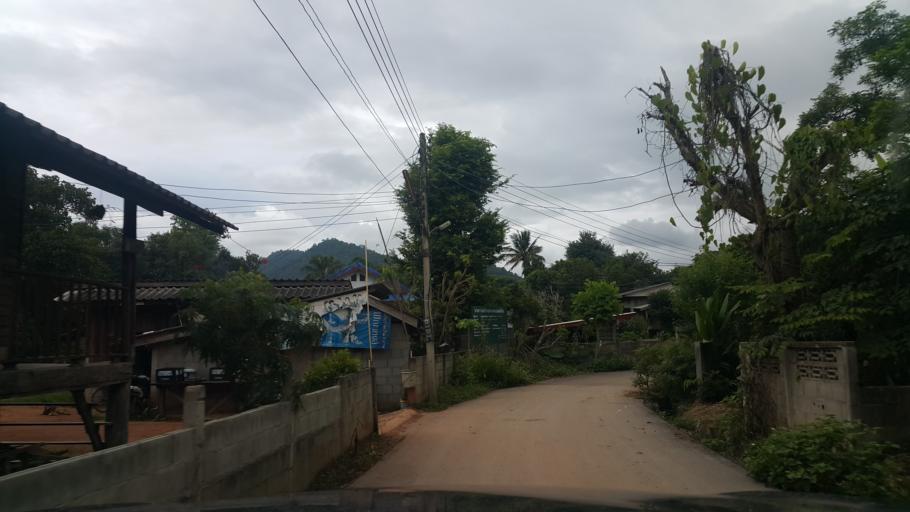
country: TH
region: Lampang
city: Wang Nuea
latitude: 19.1288
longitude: 99.4952
